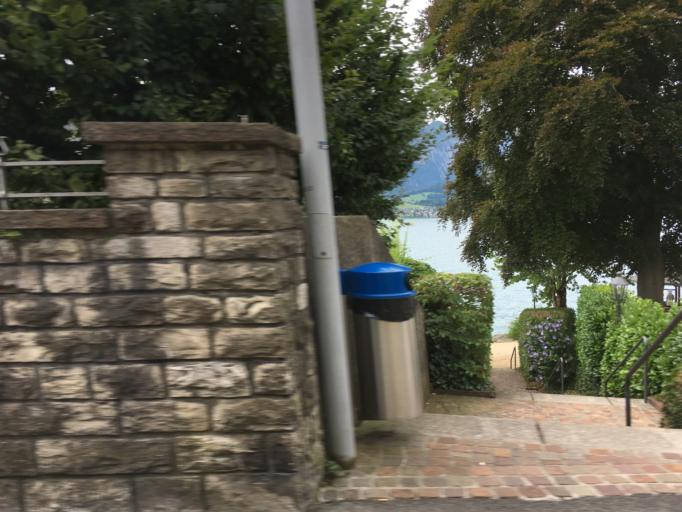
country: CH
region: Bern
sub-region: Thun District
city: Hilterfingen
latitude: 46.7350
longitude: 7.6587
